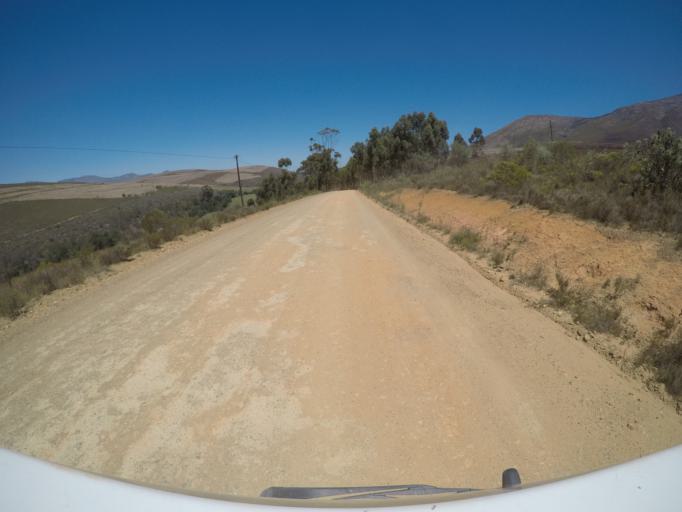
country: ZA
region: Western Cape
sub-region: Overberg District Municipality
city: Caledon
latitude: -34.1974
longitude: 19.2218
